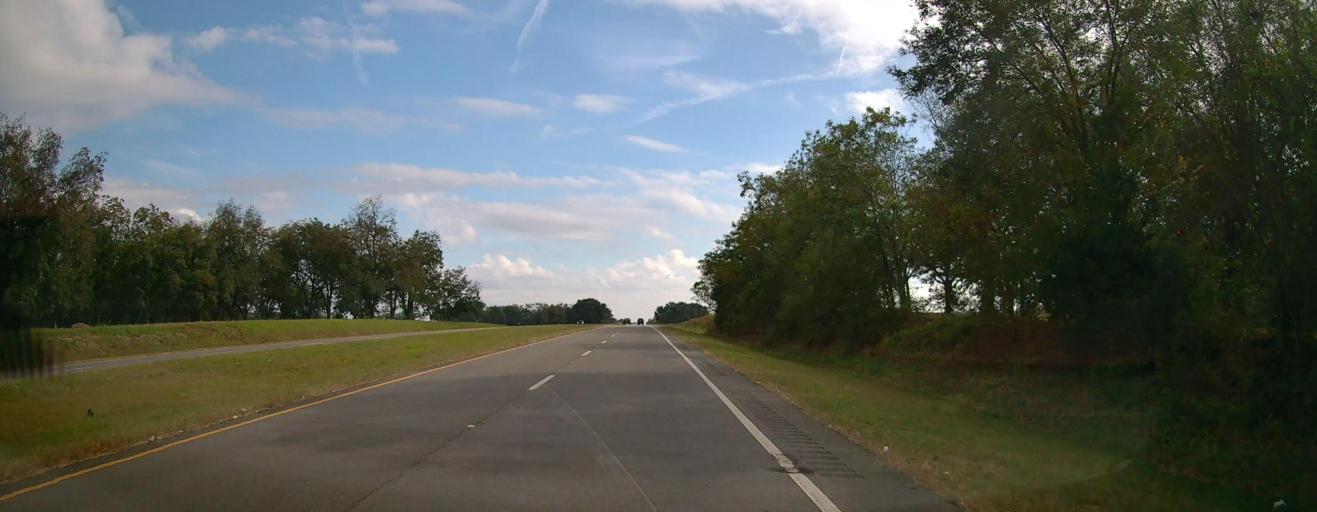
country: US
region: Georgia
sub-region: Thomas County
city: Meigs
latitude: 31.0372
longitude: -84.0658
